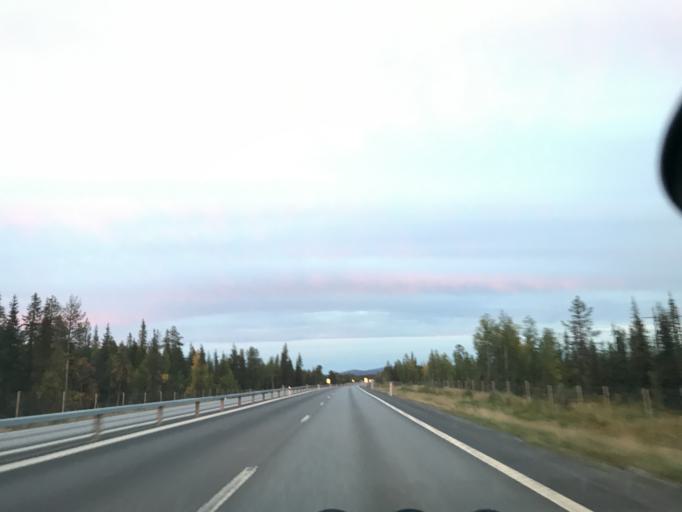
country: SE
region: Norrbotten
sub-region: Gallivare Kommun
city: Malmberget
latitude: 67.6918
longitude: 20.8266
